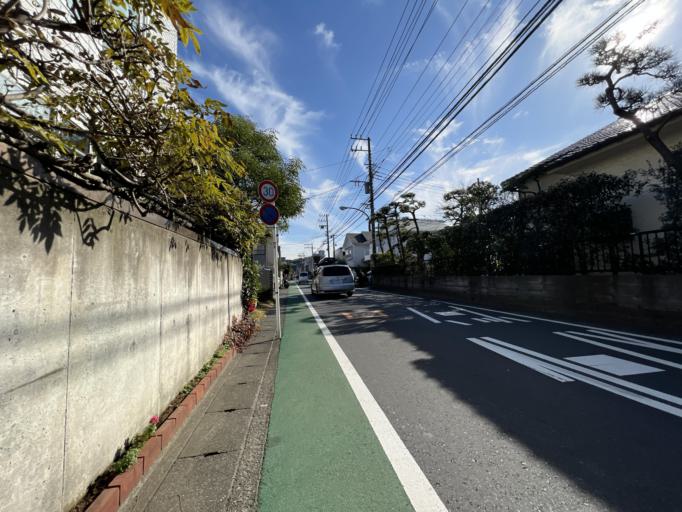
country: JP
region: Kanagawa
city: Kamakura
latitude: 35.3097
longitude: 139.5487
